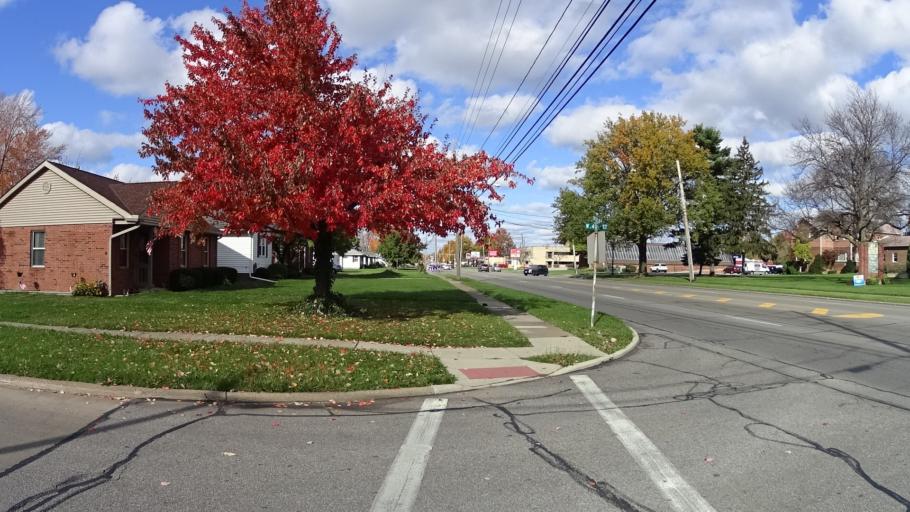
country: US
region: Ohio
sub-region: Lorain County
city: Lorain
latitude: 41.4344
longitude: -82.1856
